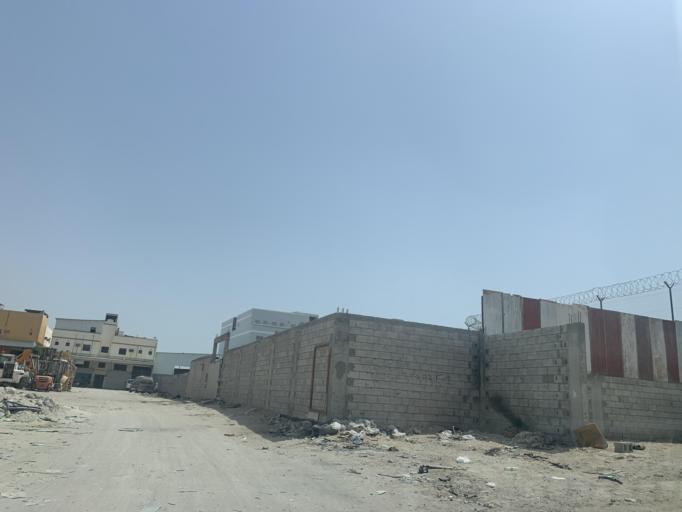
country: BH
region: Central Governorate
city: Madinat Hamad
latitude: 26.1422
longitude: 50.4820
